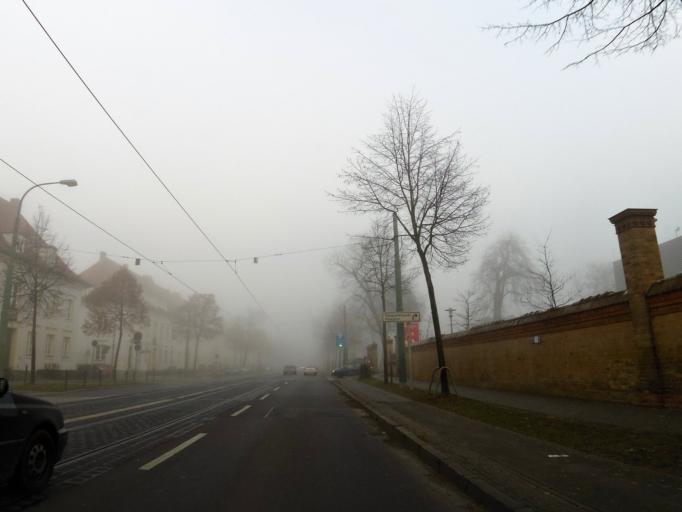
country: DE
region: Brandenburg
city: Potsdam
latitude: 52.3816
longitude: 13.0180
